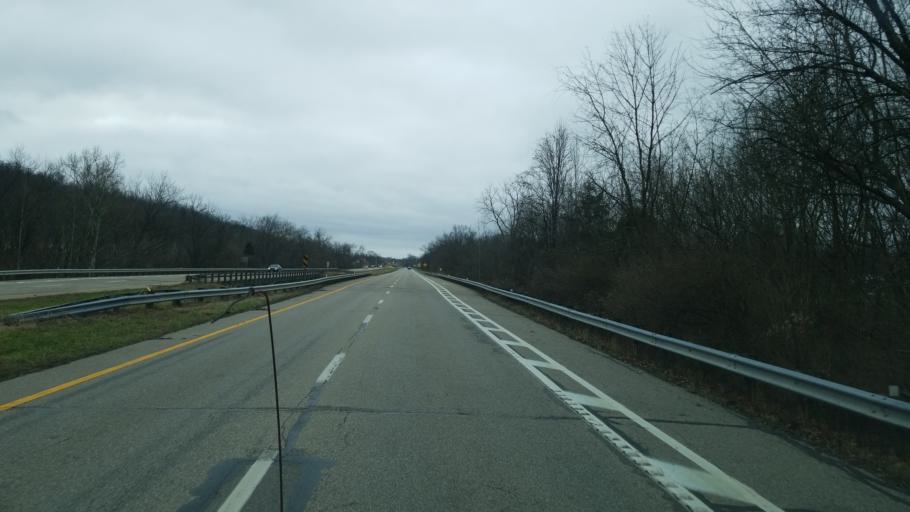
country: US
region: Ohio
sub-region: Clermont County
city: New Richmond
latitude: 38.9615
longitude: -84.2842
